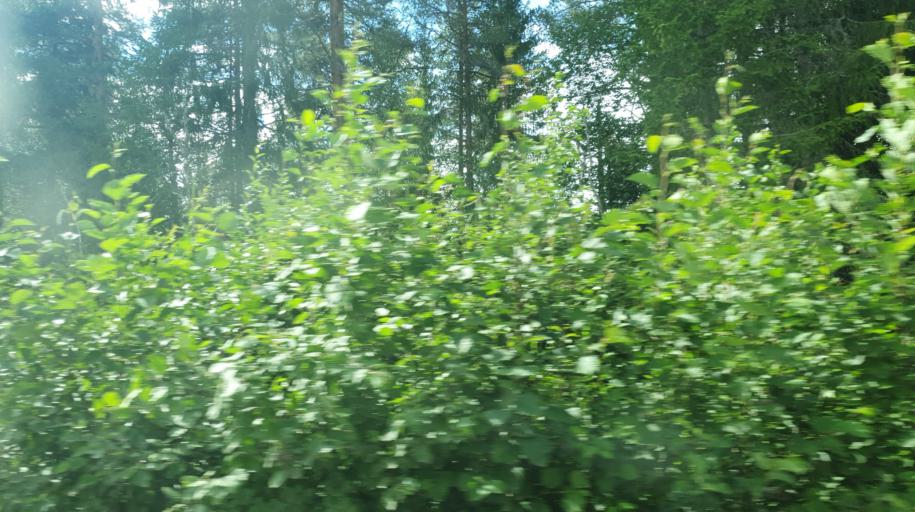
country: NO
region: Nord-Trondelag
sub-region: Levanger
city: Skogn
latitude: 63.5812
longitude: 11.2466
